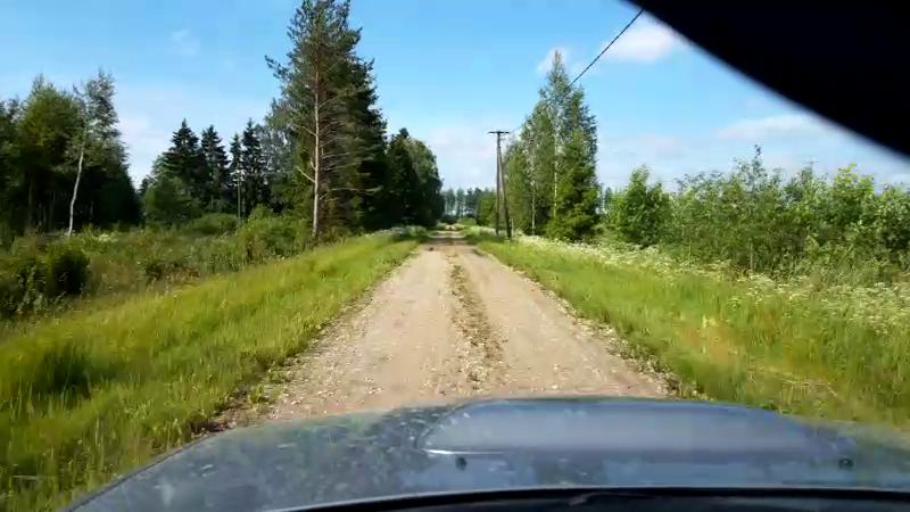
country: EE
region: Paernumaa
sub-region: Sindi linn
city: Sindi
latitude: 58.4875
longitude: 24.6674
